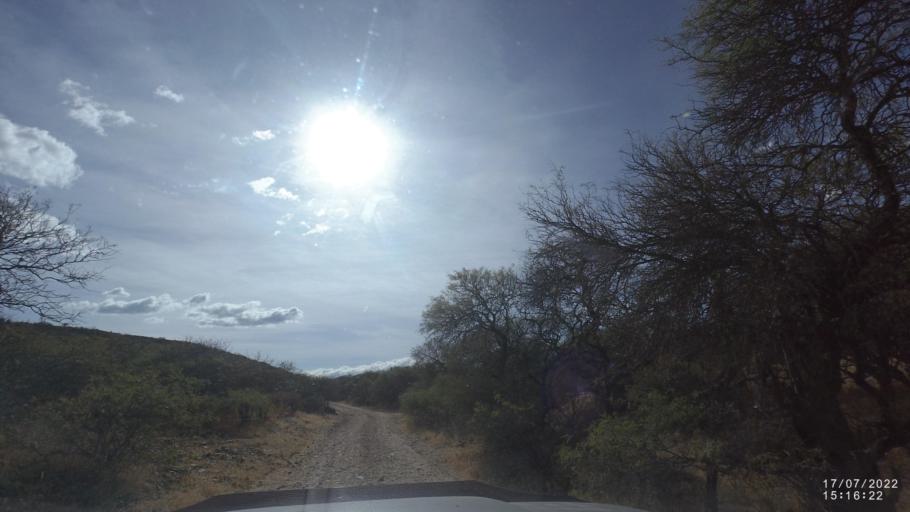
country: BO
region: Cochabamba
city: Capinota
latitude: -17.5544
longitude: -66.2641
